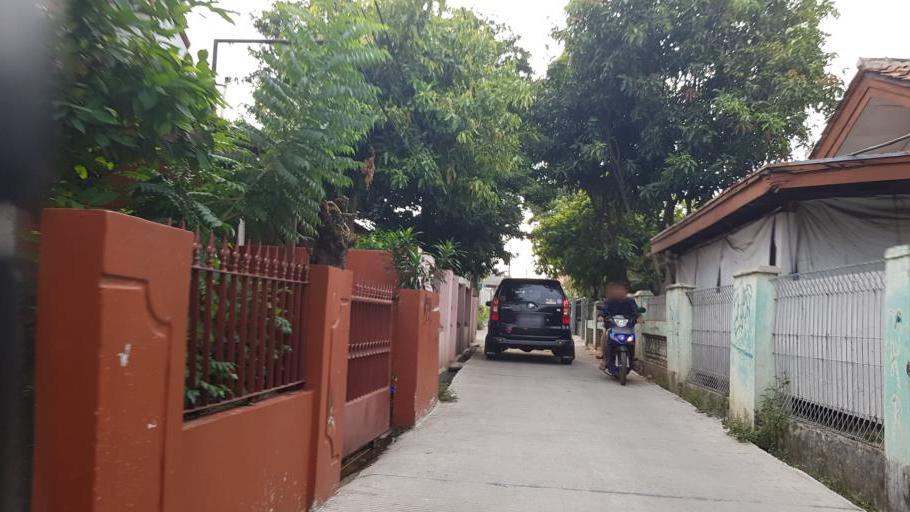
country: ID
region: West Java
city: Depok
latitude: -6.3934
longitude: 106.7987
